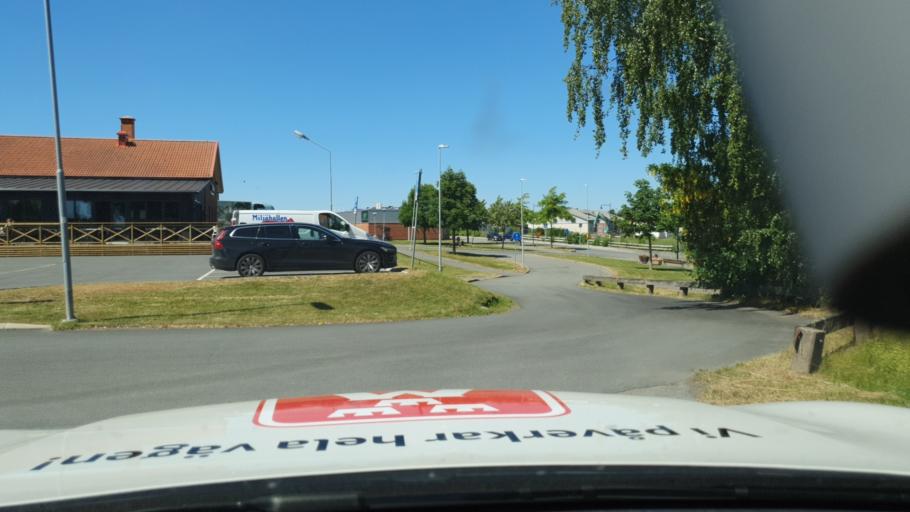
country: SE
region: Joenkoeping
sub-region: Habo Kommun
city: Habo
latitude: 57.9064
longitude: 14.0783
